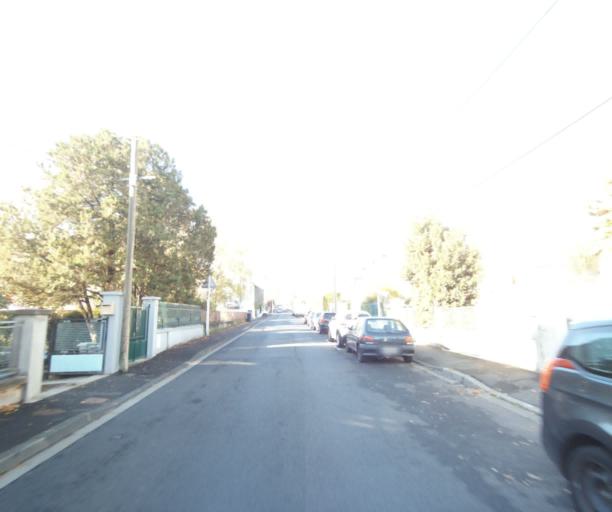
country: FR
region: Auvergne
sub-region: Departement du Puy-de-Dome
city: Clermont-Ferrand
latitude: 45.7943
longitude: 3.0866
